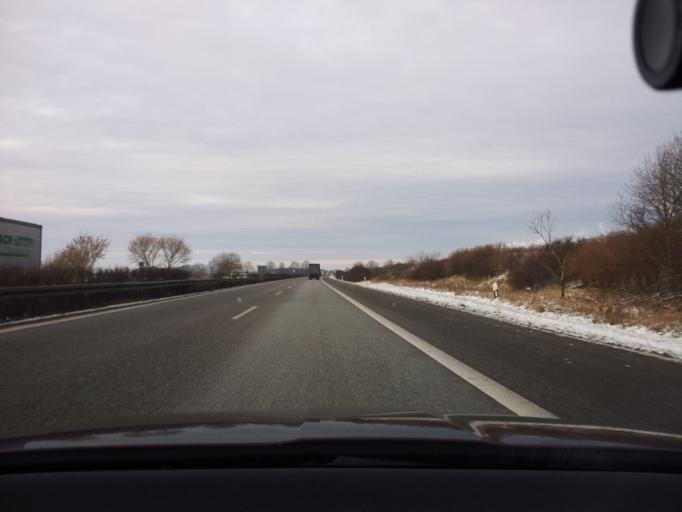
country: DE
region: Mecklenburg-Vorpommern
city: Wittenburg
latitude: 53.4983
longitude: 11.0843
